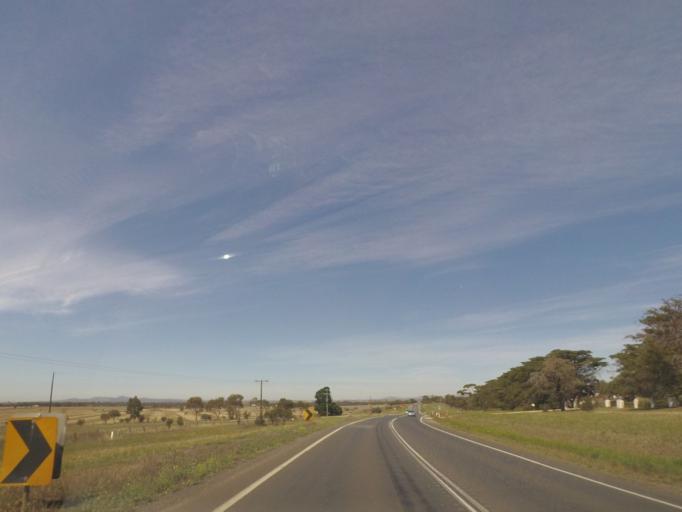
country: AU
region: Victoria
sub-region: Moorabool
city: Bacchus Marsh
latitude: -37.7755
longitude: 144.4378
